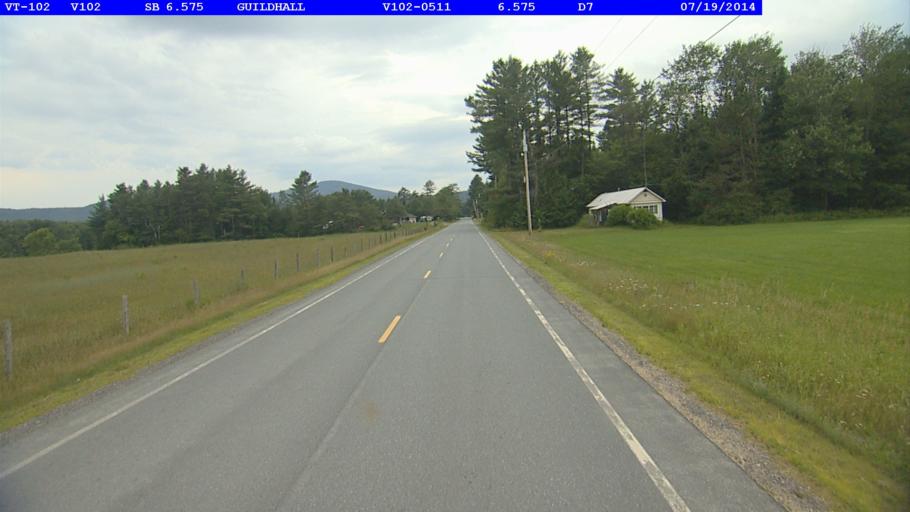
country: US
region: Vermont
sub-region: Essex County
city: Guildhall
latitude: 44.5661
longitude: -71.5738
